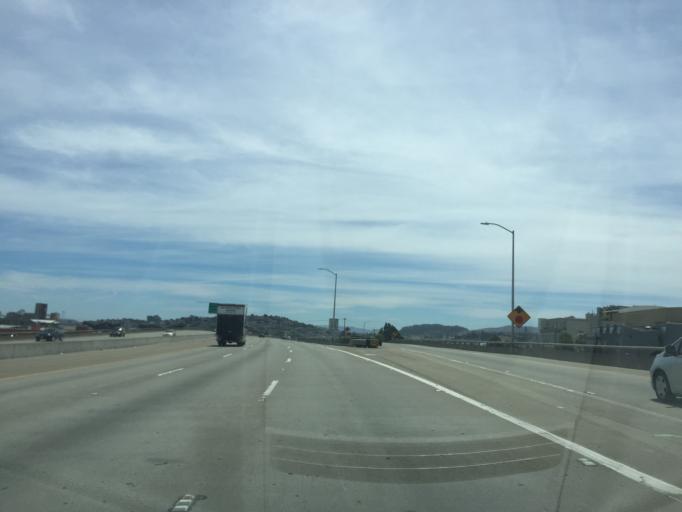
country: US
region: California
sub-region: San Francisco County
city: San Francisco
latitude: 37.7559
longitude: -122.3925
